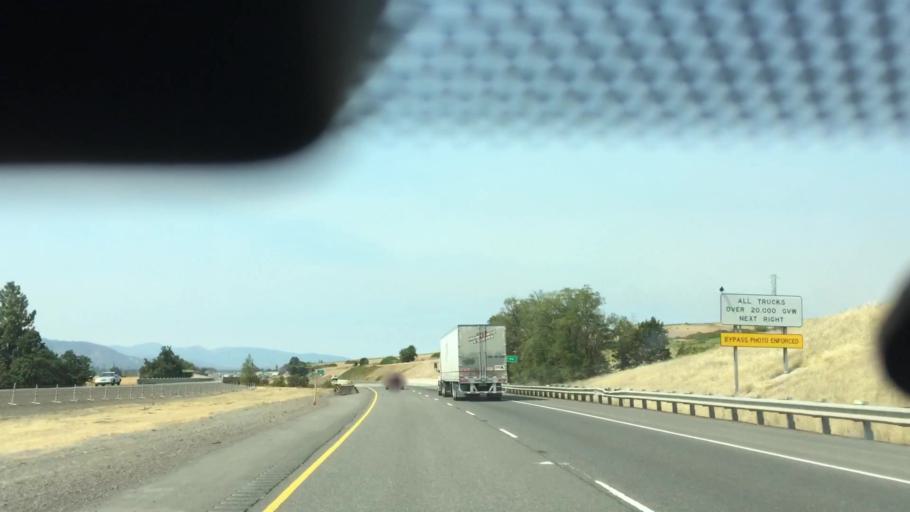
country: US
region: Oregon
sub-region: Jackson County
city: Ashland
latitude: 42.2155
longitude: -122.7072
